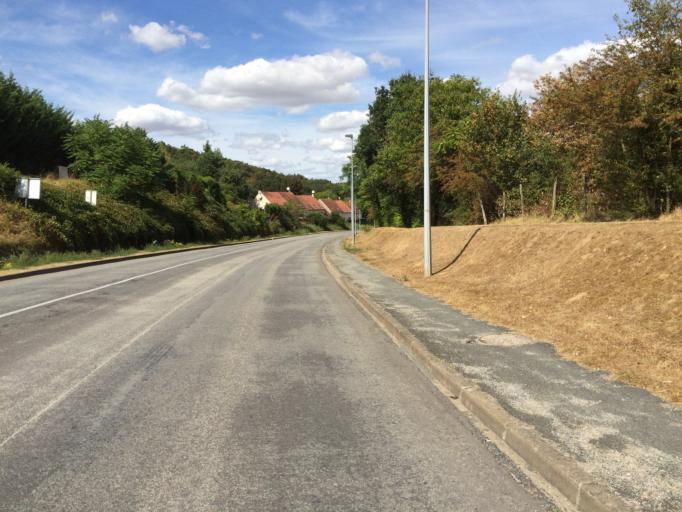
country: FR
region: Ile-de-France
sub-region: Departement de l'Essonne
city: Maisse
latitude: 48.3982
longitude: 2.3759
